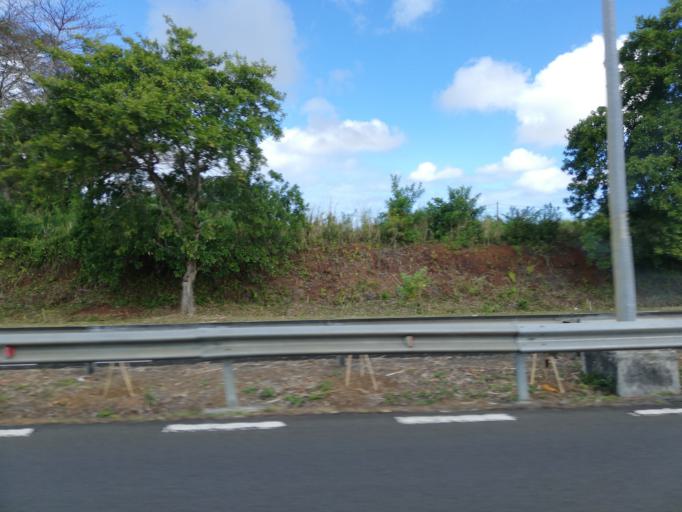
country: MU
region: Grand Port
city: Plaine Magnien
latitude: -20.4228
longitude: 57.6566
